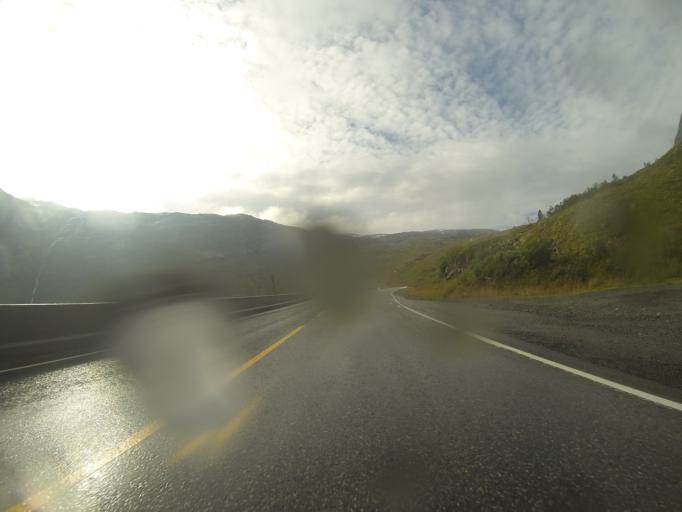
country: NO
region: Hordaland
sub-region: Odda
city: Odda
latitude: 59.8220
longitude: 6.7434
